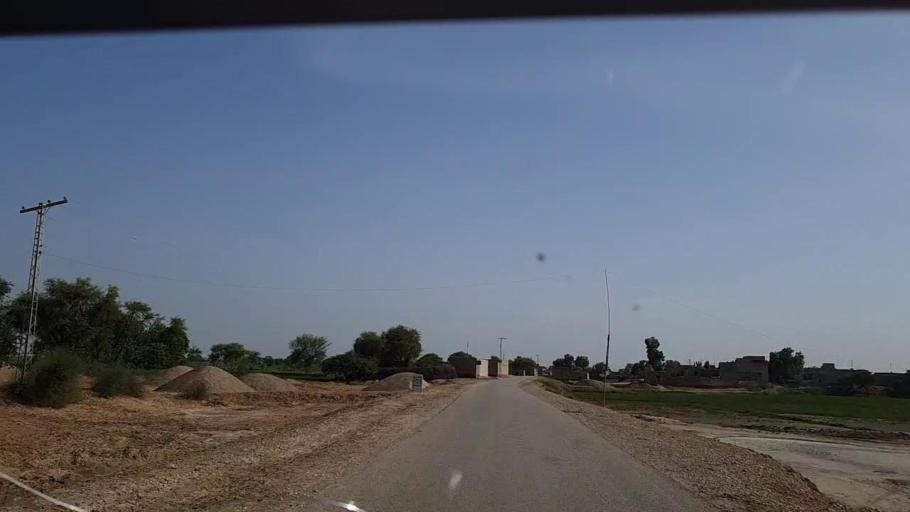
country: PK
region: Sindh
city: Khairpur Nathan Shah
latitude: 26.9984
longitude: 67.6665
